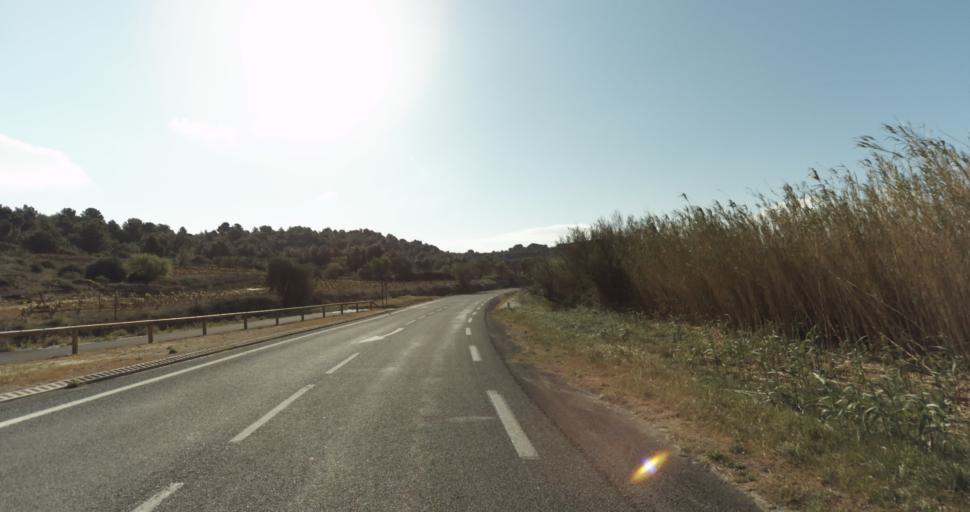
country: FR
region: Languedoc-Roussillon
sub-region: Departement de l'Aude
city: Leucate
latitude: 42.9279
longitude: 3.0126
